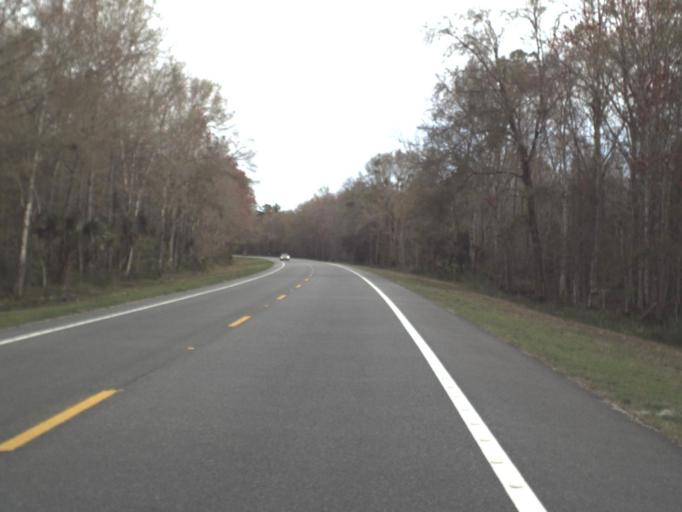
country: US
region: Florida
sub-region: Leon County
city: Woodville
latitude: 30.1601
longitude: -84.0012
